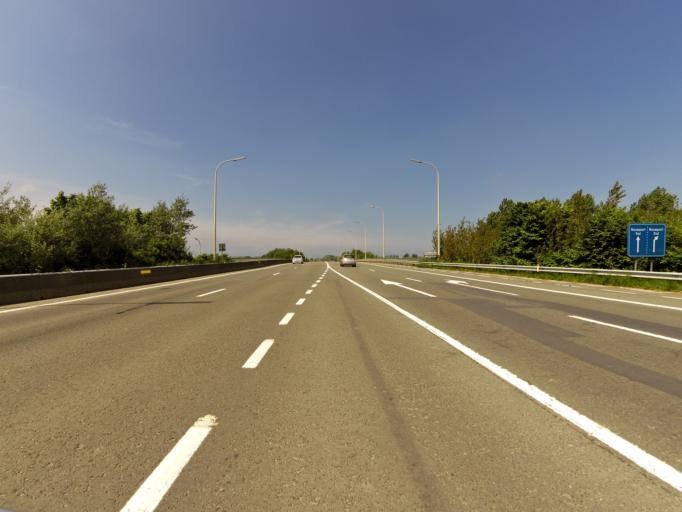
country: BE
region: Flanders
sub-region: Provincie West-Vlaanderen
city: Nieuwpoort
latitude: 51.1198
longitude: 2.7468
